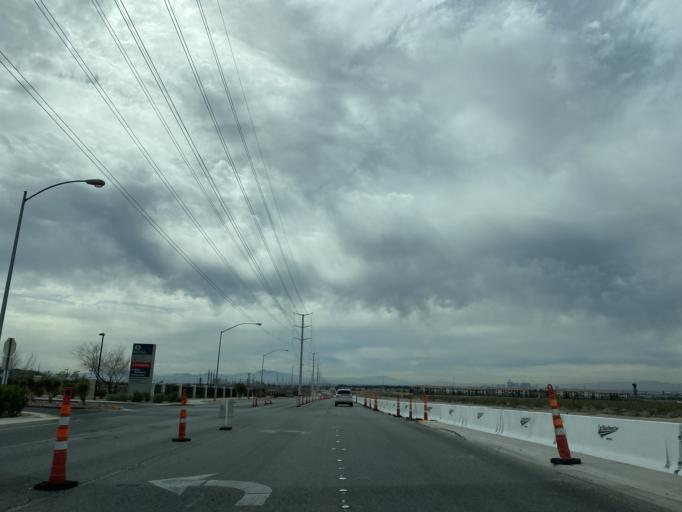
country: US
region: Nevada
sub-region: Clark County
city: Nellis Air Force Base
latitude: 36.2863
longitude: -115.0987
